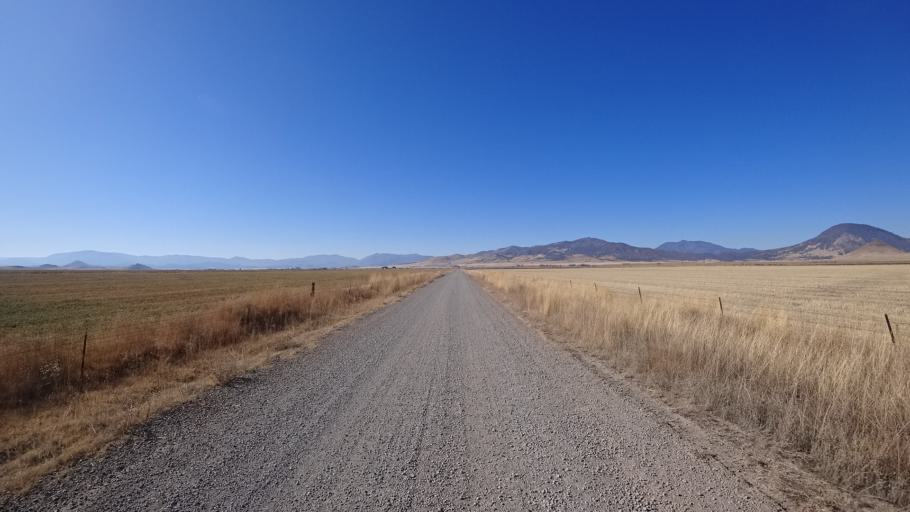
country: US
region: California
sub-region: Siskiyou County
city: Montague
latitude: 41.7865
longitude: -122.4430
